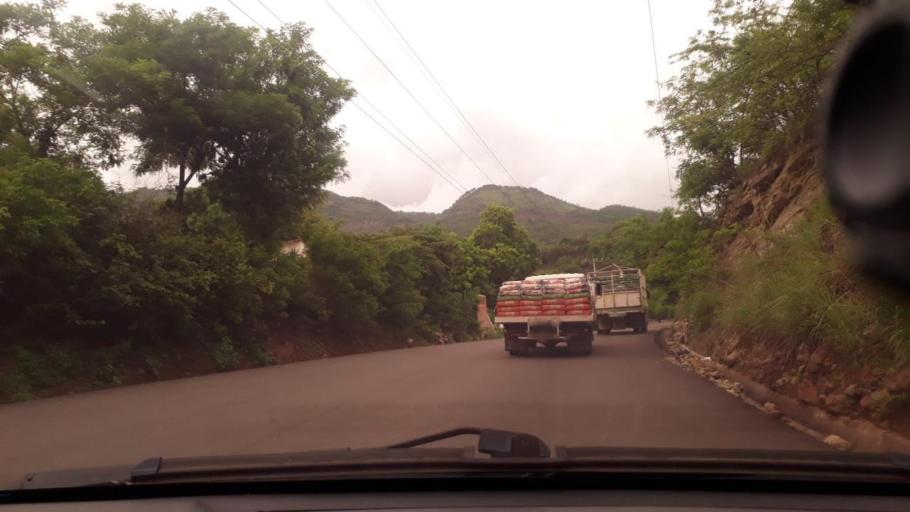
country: GT
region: Chiquimula
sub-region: Municipio de San Juan Ermita
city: San Juan Ermita
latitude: 14.7360
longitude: -89.4726
